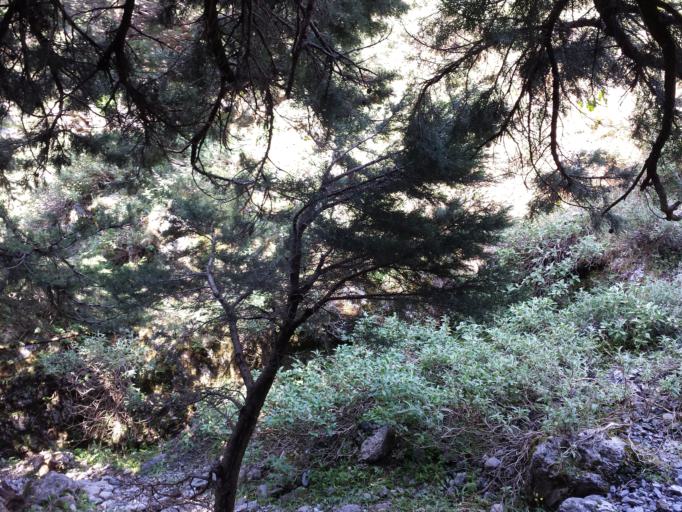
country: GR
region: Crete
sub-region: Nomos Chanias
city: Chora Sfakion
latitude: 35.2345
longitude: 24.1633
